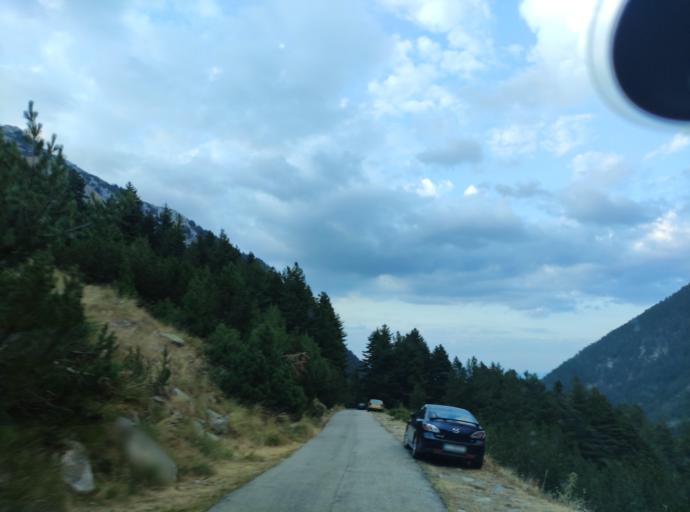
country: BG
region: Blagoevgrad
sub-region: Obshtina Bansko
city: Bansko
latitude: 41.7603
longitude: 23.4166
